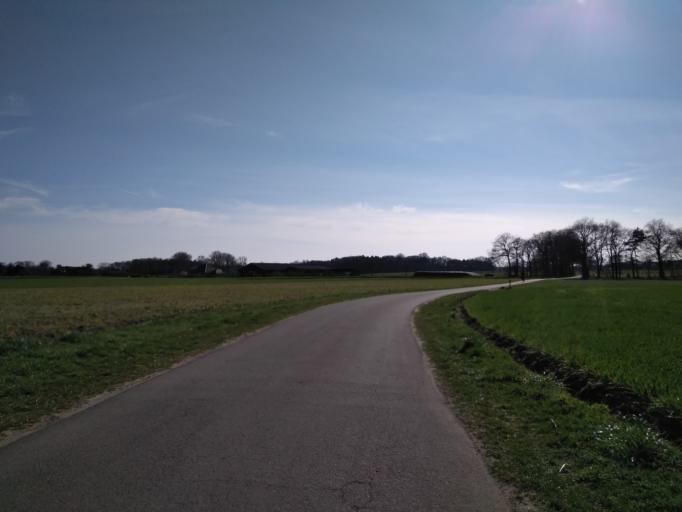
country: DE
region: North Rhine-Westphalia
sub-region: Regierungsbezirk Dusseldorf
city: Schermbeck
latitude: 51.6559
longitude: 6.8680
